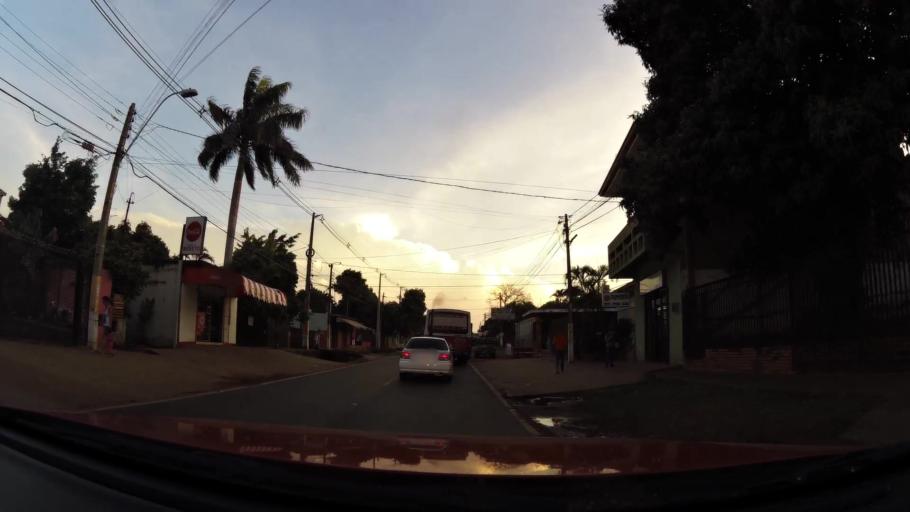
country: PY
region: Central
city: San Lorenzo
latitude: -25.3756
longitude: -57.4923
